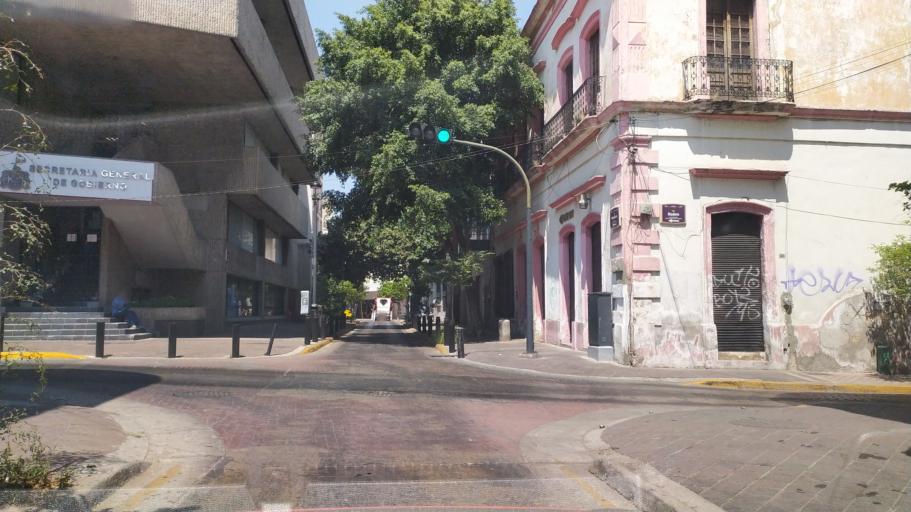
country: MX
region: Jalisco
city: Guadalajara
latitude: 20.6735
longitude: -103.3450
